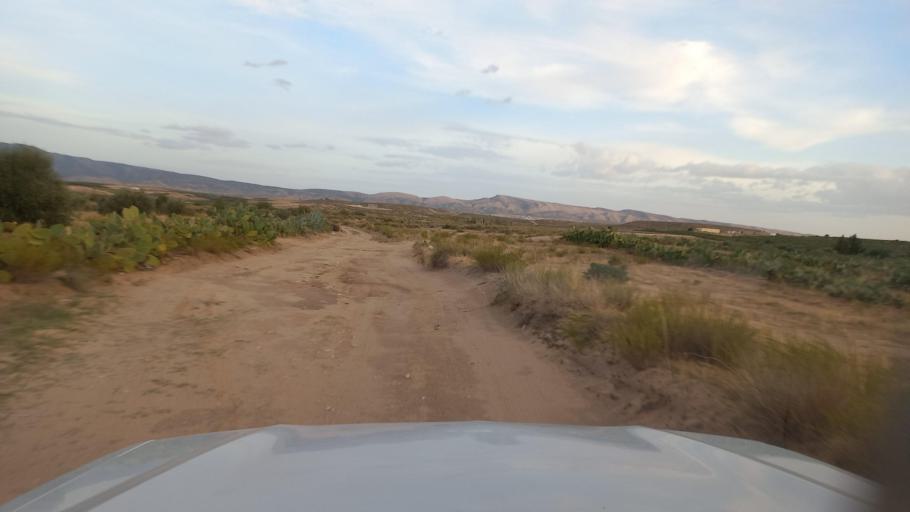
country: TN
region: Al Qasrayn
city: Sbiba
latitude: 35.4110
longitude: 9.0832
